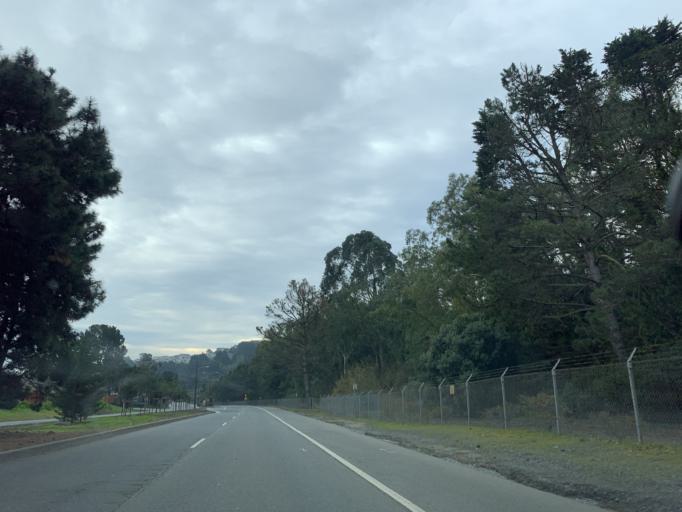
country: US
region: California
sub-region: San Mateo County
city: Colma
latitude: 37.6499
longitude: -122.4510
